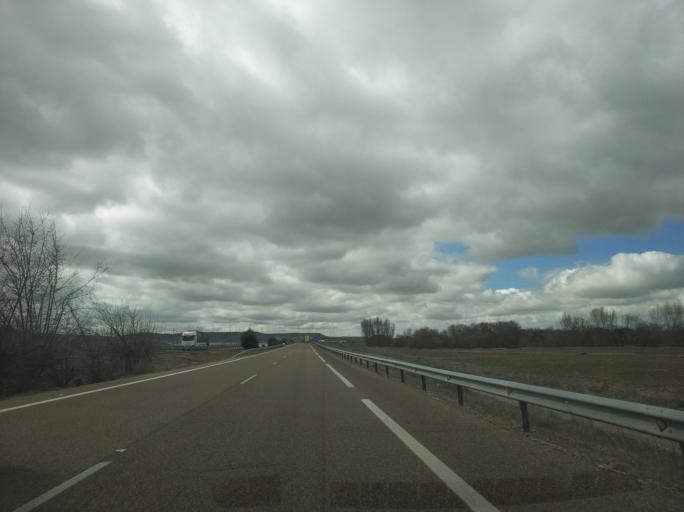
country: ES
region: Castille and Leon
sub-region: Provincia de Palencia
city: Cordovilla la Real
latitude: 42.0605
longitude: -4.2342
